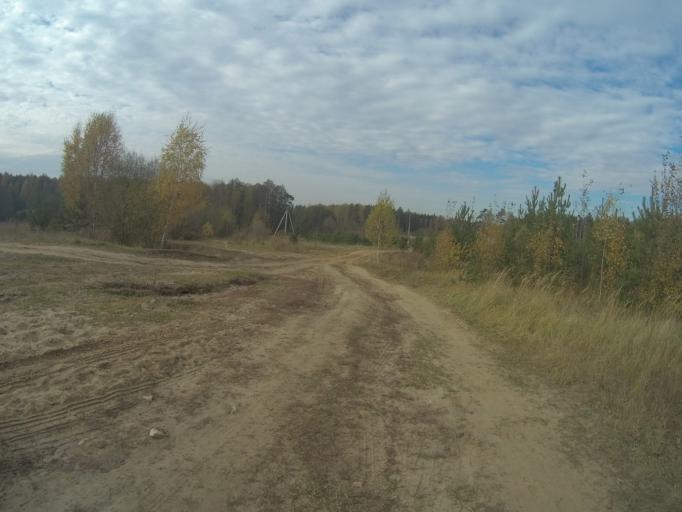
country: RU
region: Vladimir
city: Kommunar
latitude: 56.0858
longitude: 40.4918
